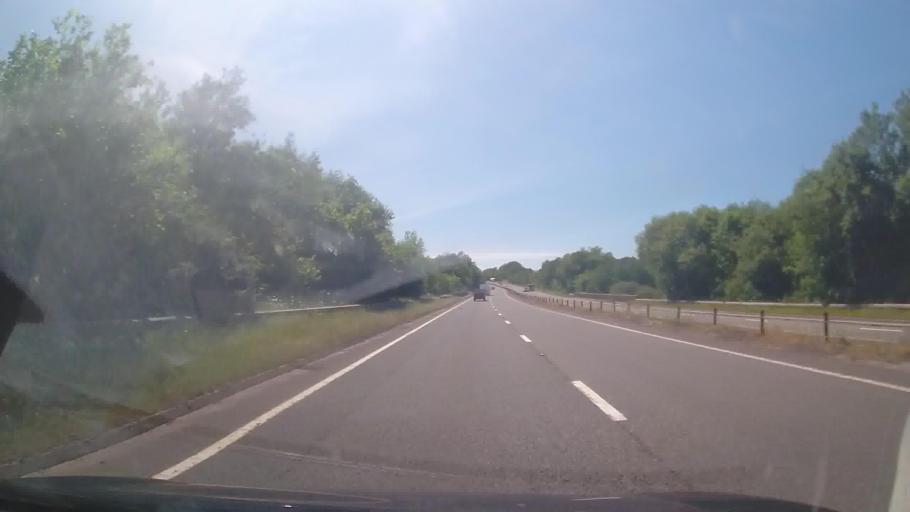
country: GB
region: England
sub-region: Devon
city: Ottery St Mary
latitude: 50.7823
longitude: -3.2545
